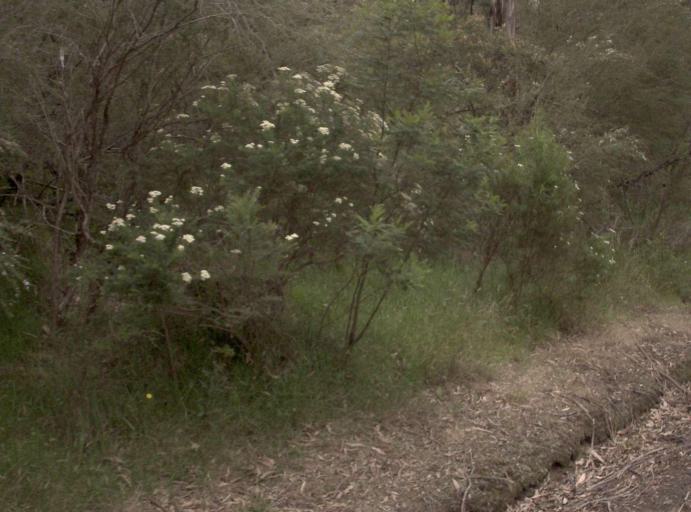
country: AU
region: New South Wales
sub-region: Bombala
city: Bombala
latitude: -37.3969
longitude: 149.1959
